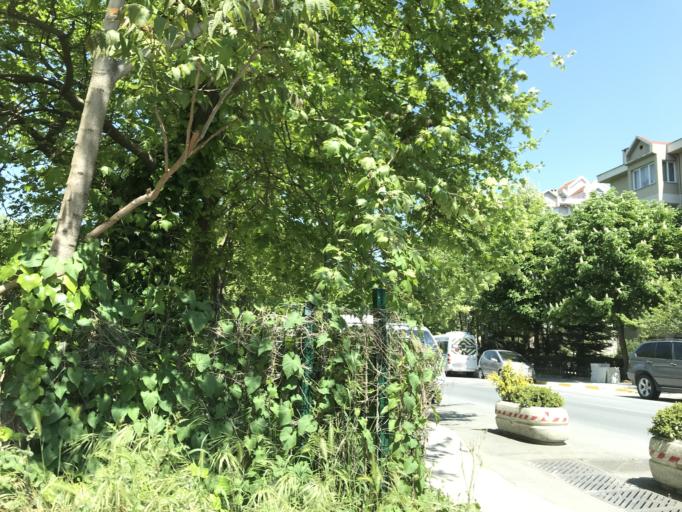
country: TR
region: Istanbul
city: Esenyurt
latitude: 41.0563
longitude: 28.6744
